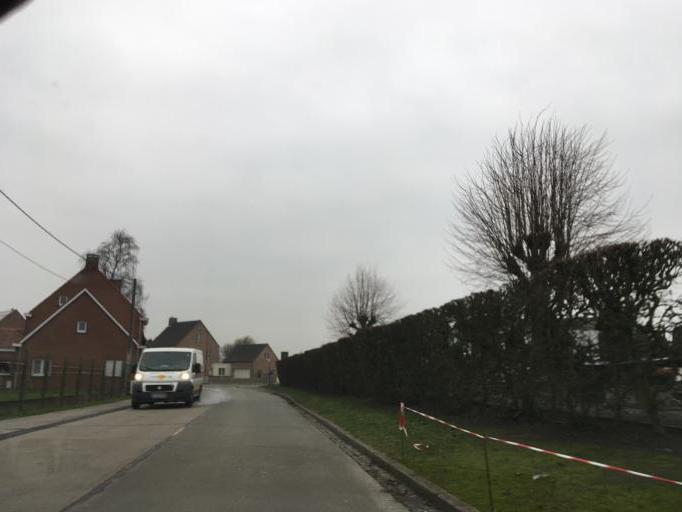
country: BE
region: Flanders
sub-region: Provincie West-Vlaanderen
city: Ardooie
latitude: 50.9760
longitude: 3.2058
